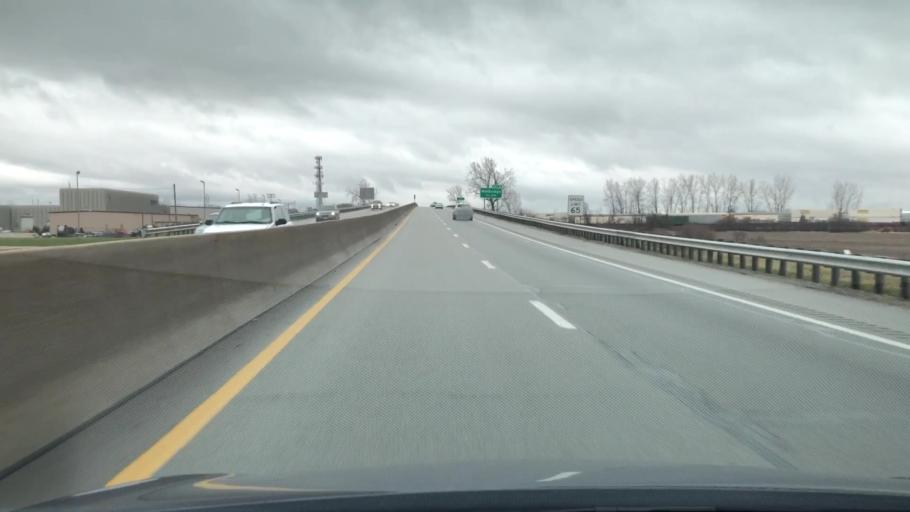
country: US
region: Ohio
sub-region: Wood County
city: Northwood
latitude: 41.6025
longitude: -83.4769
